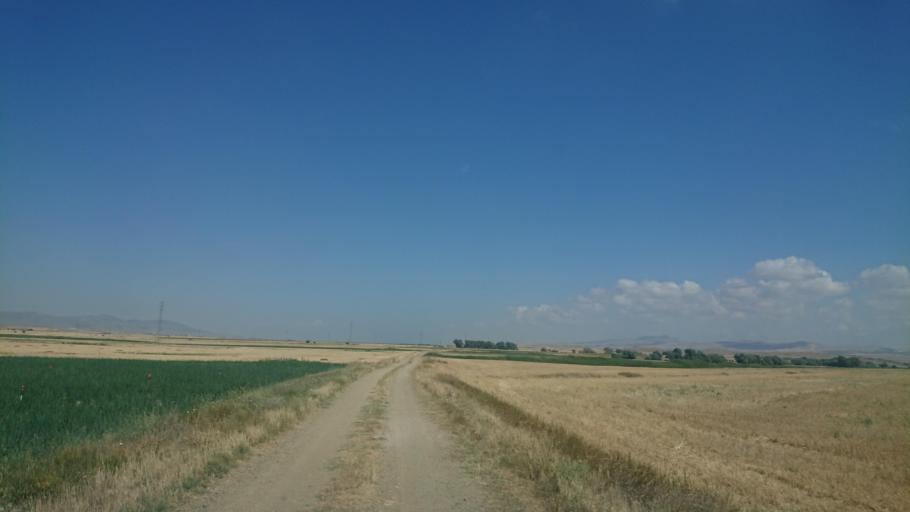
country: TR
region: Aksaray
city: Sariyahsi
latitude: 38.9894
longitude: 33.9015
